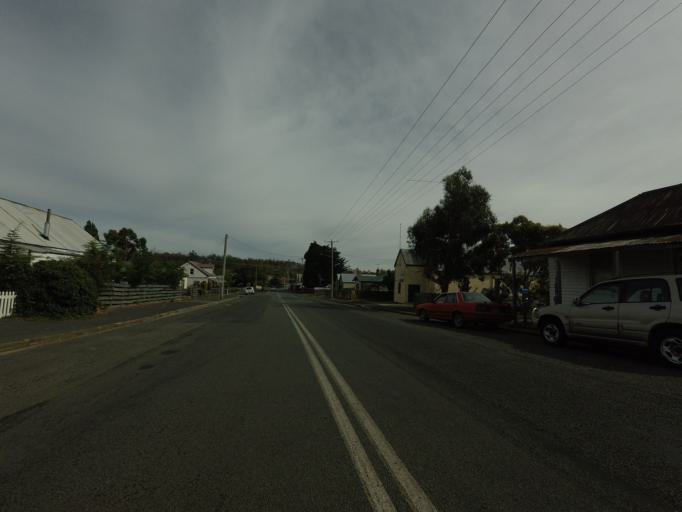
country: AU
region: Tasmania
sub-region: Brighton
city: Bridgewater
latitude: -42.3503
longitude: 147.4066
